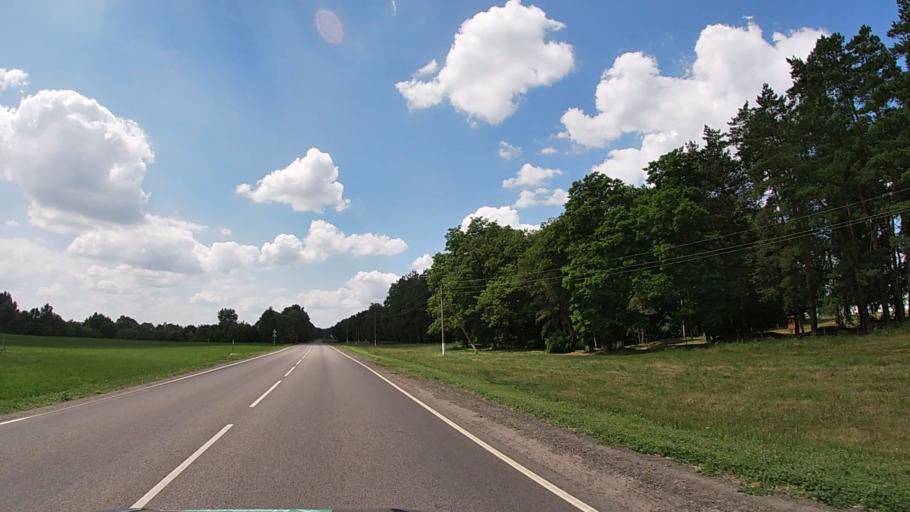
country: RU
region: Belgorod
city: Grayvoron
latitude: 50.5001
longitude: 35.7224
